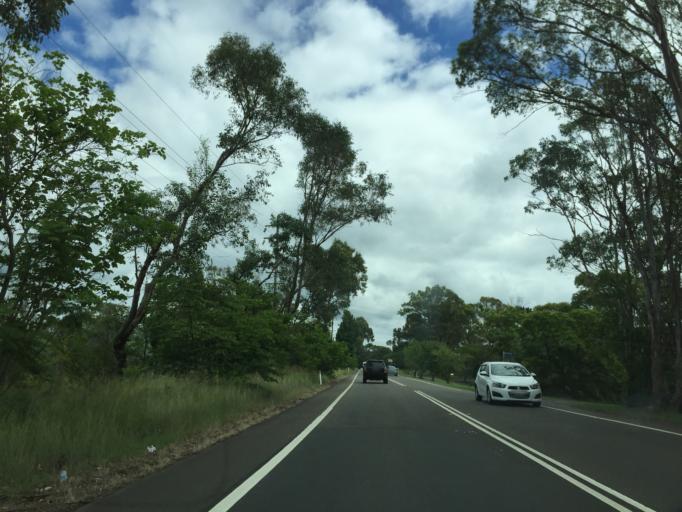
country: AU
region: New South Wales
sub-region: Hawkesbury
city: Richmond
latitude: -33.5580
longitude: 150.7008
